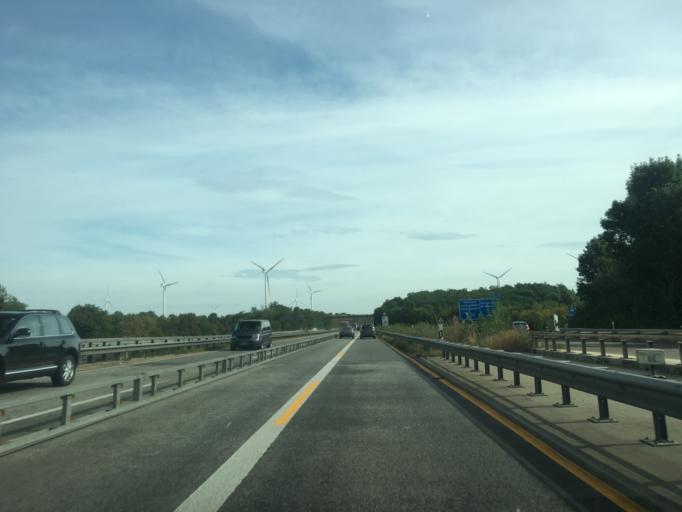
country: DE
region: Rheinland-Pfalz
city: Morstadt
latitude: 49.6658
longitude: 8.2726
